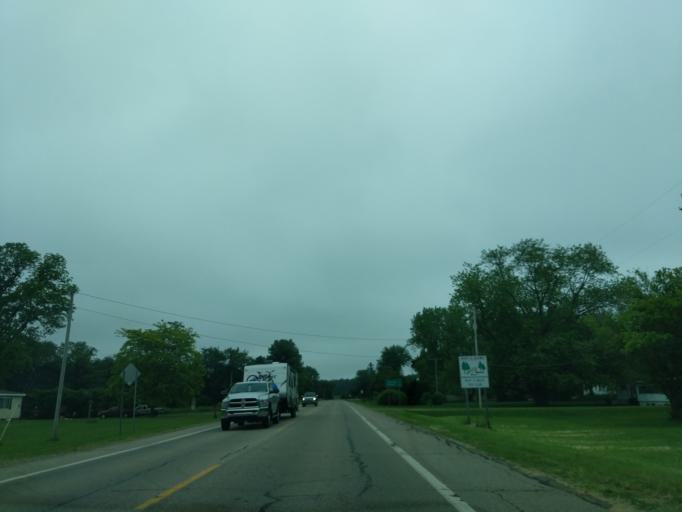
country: US
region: Michigan
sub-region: Hillsdale County
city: Litchfield
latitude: 42.0385
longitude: -84.7436
